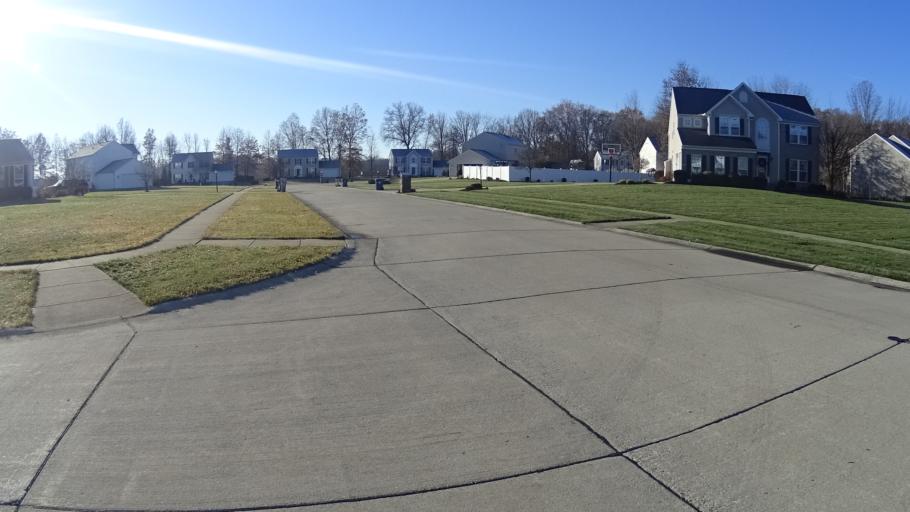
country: US
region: Ohio
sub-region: Lorain County
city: Sheffield Lake
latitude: 41.4569
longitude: -82.0819
